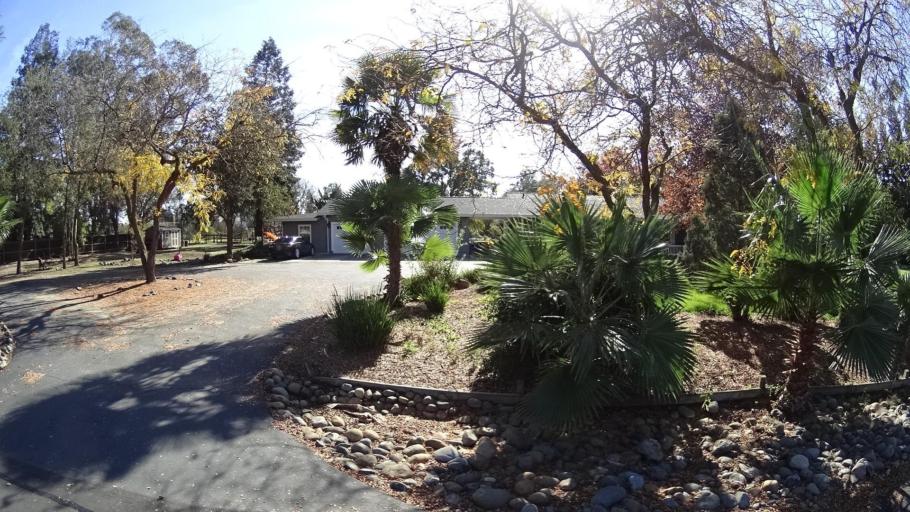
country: US
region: California
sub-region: Sacramento County
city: Vineyard
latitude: 38.4372
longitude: -121.3175
